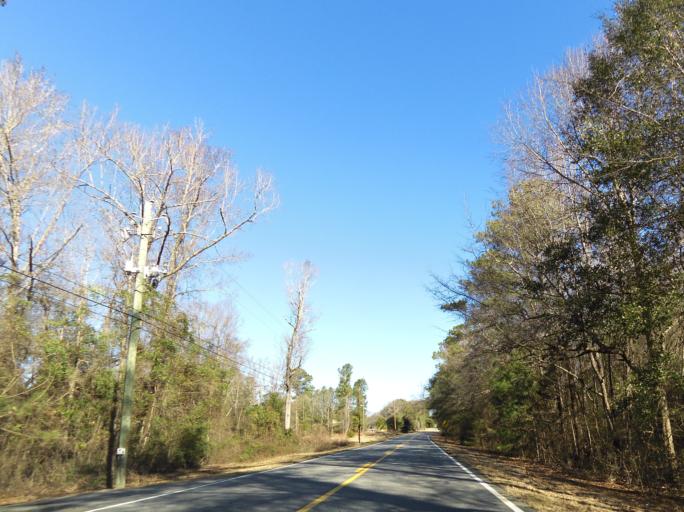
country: US
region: Georgia
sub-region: Bibb County
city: West Point
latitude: 32.7839
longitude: -83.7568
